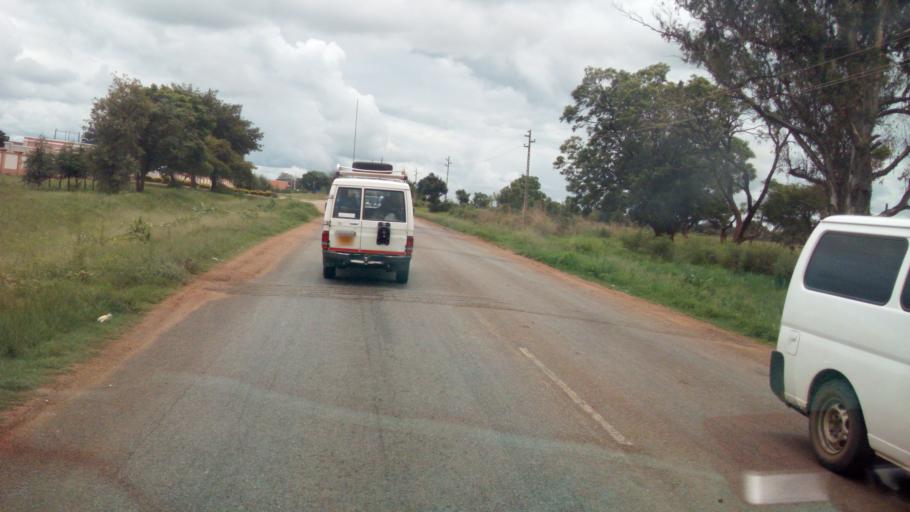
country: ZW
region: Harare
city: Harare
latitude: -17.7327
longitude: 31.0234
